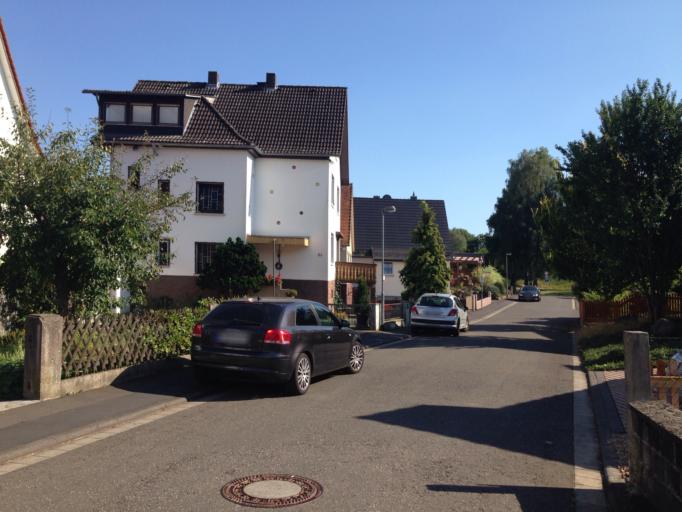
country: DE
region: Hesse
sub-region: Regierungsbezirk Giessen
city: Rabenau
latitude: 50.6590
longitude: 8.8908
